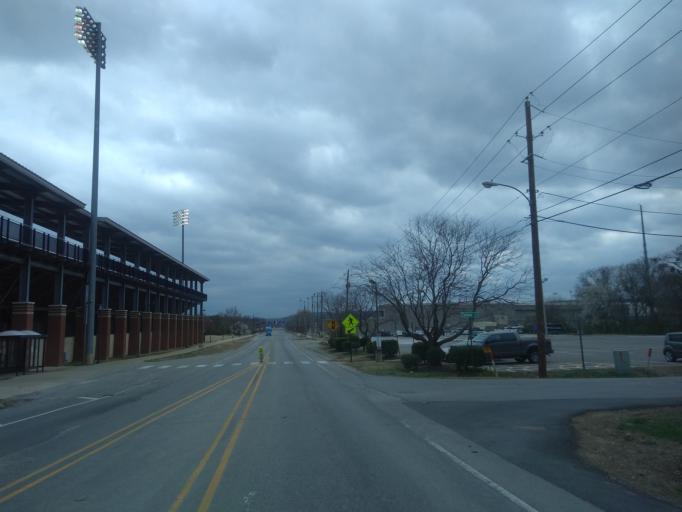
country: US
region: Arkansas
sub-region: Washington County
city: Fayetteville
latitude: 36.0633
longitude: -94.1803
